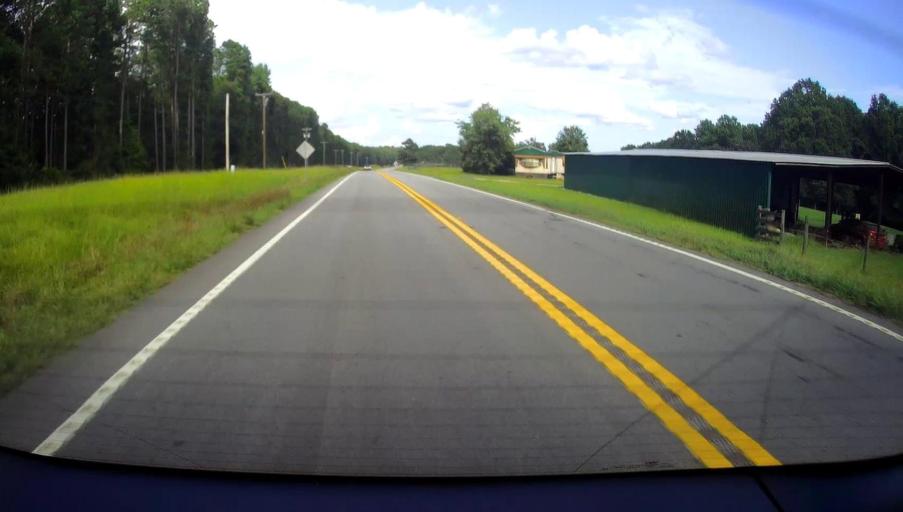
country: US
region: Georgia
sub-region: Meriwether County
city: Manchester
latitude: 32.9864
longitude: -84.5400
